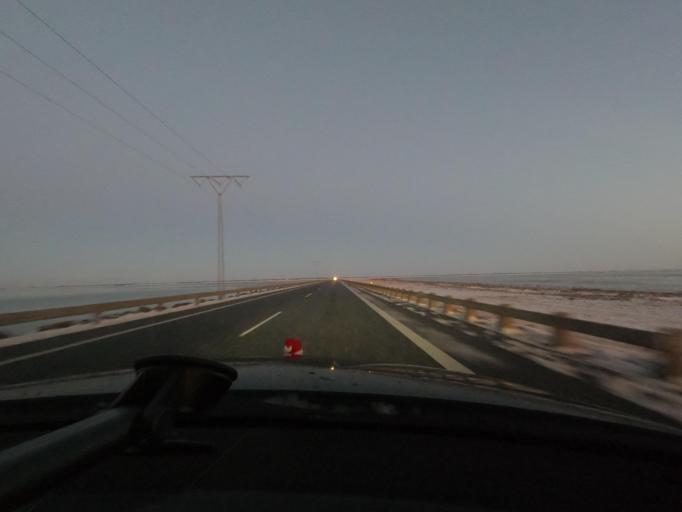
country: DK
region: South Denmark
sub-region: Tonder Kommune
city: Sherrebek
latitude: 55.1488
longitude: 8.6384
